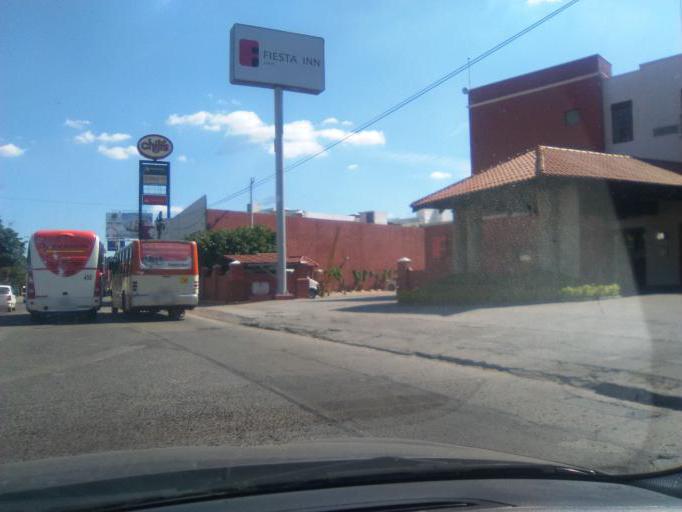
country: MX
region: Guanajuato
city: Leon
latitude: 21.1033
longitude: -101.6372
